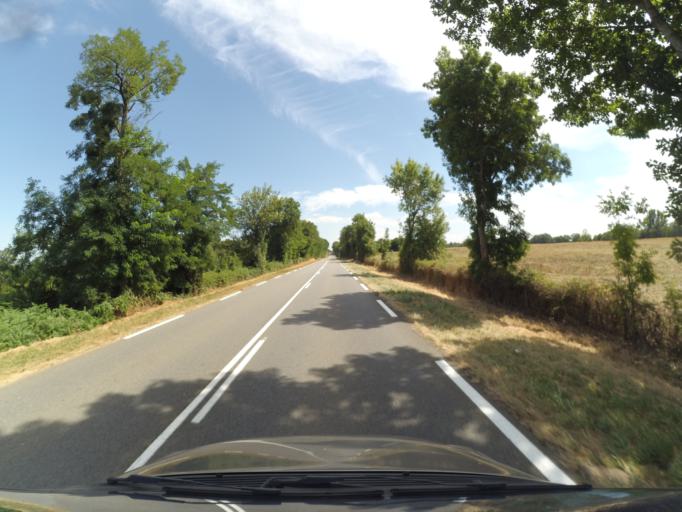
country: FR
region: Poitou-Charentes
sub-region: Departement de la Charente
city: Confolens
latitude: 45.9875
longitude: 0.6753
